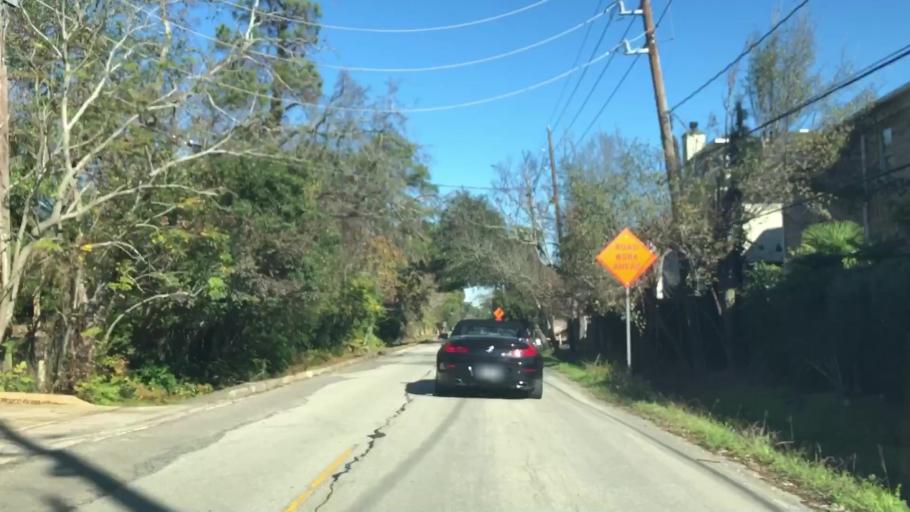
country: US
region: Texas
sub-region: Harris County
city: Hunters Creek Village
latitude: 29.7587
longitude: -95.4676
